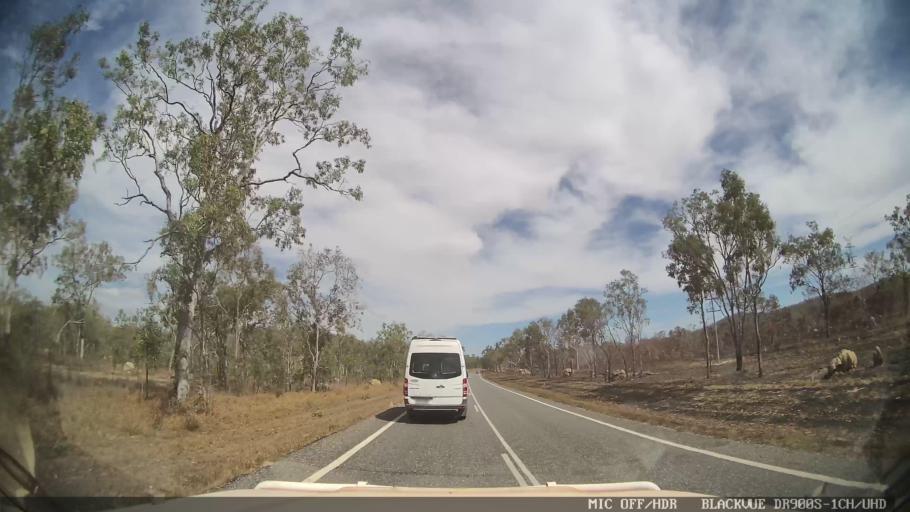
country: AU
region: Queensland
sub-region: Cairns
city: Port Douglas
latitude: -16.7228
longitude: 145.3530
